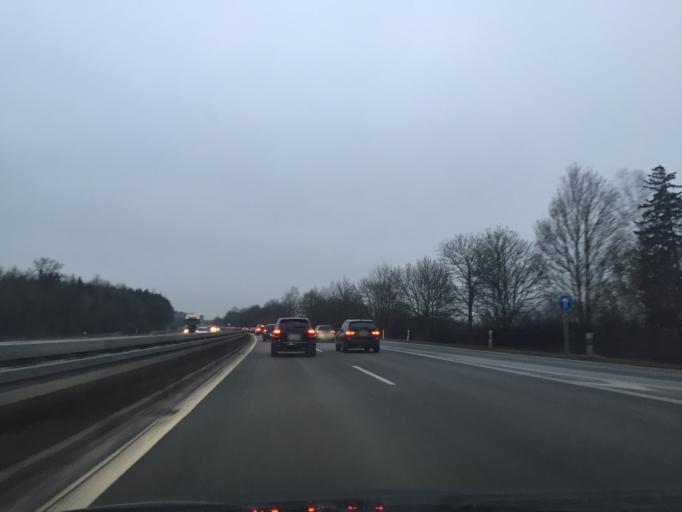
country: DE
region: Bavaria
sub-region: Upper Bavaria
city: Germering
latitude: 48.1082
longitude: 11.3443
